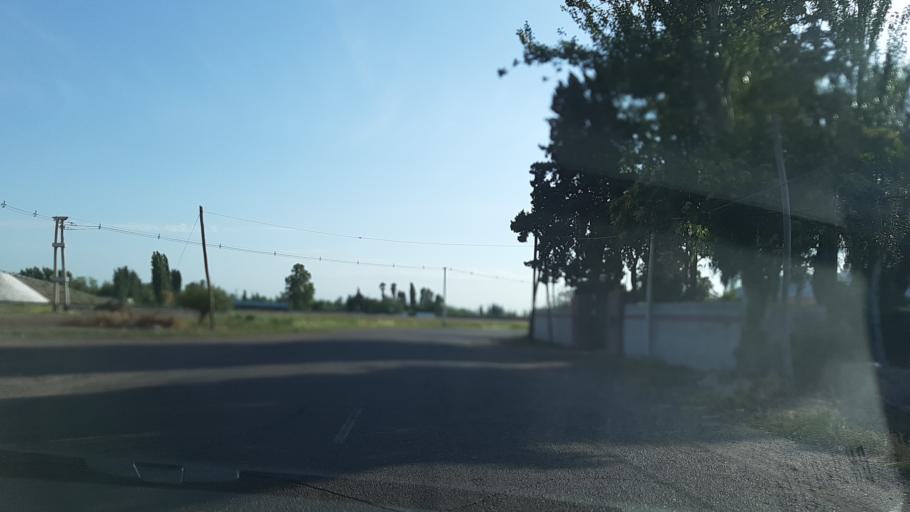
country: AR
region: Mendoza
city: San Martin
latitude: -33.0420
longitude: -68.5208
